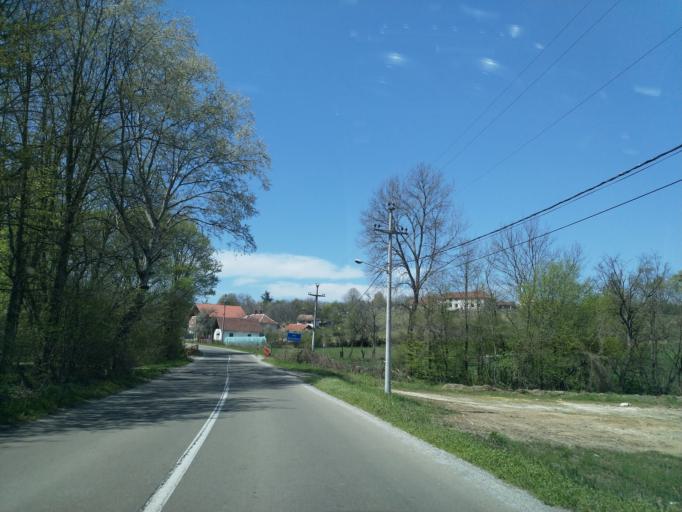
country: RS
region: Central Serbia
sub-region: Belgrade
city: Lazarevac
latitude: 44.3527
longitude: 20.3772
